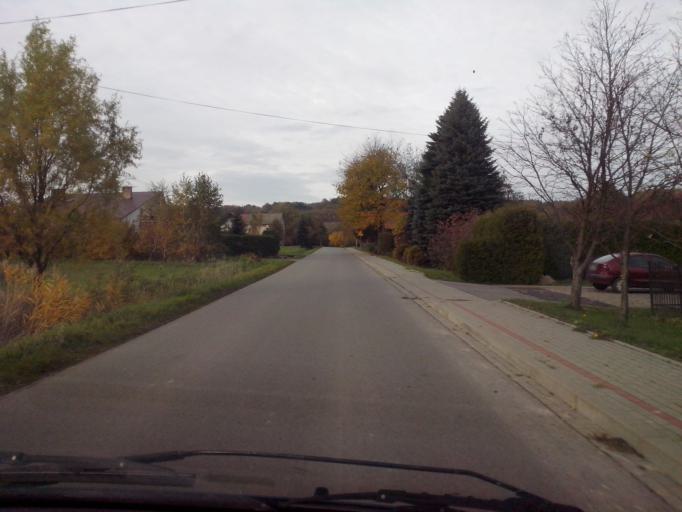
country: PL
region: Subcarpathian Voivodeship
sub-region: Powiat strzyzowski
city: Wisniowa
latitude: 49.8738
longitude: 21.6803
